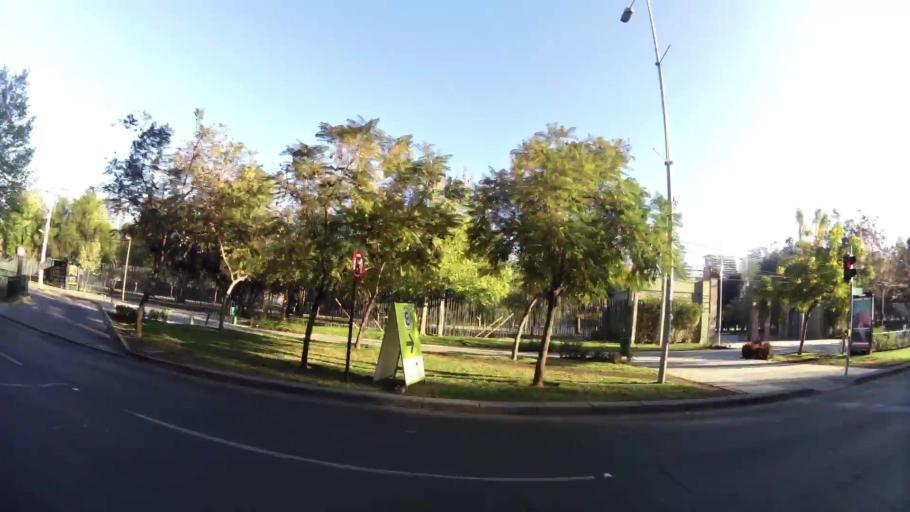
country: CL
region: Santiago Metropolitan
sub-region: Provincia de Santiago
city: Villa Presidente Frei, Nunoa, Santiago, Chile
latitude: -33.4040
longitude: -70.5736
